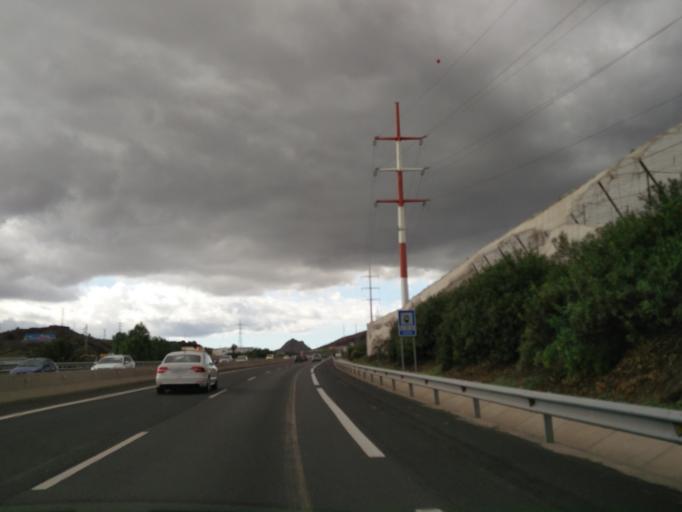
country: ES
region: Canary Islands
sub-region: Provincia de Santa Cruz de Tenerife
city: Las Rosas
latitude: 28.0500
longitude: -16.6317
